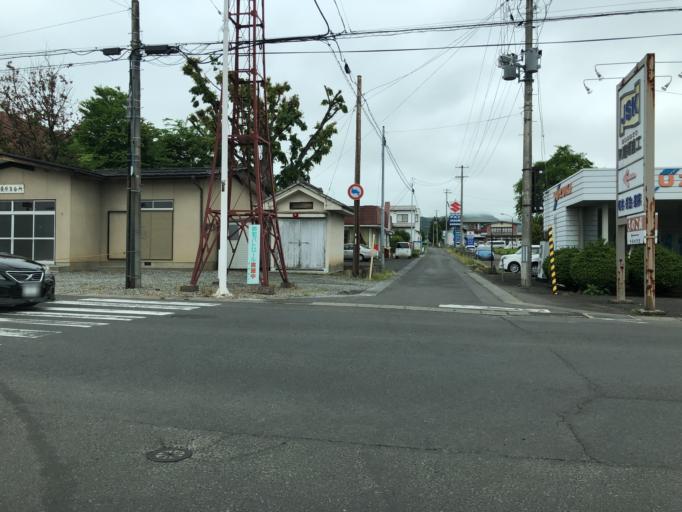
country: JP
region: Fukushima
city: Fukushima-shi
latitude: 37.7759
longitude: 140.3928
